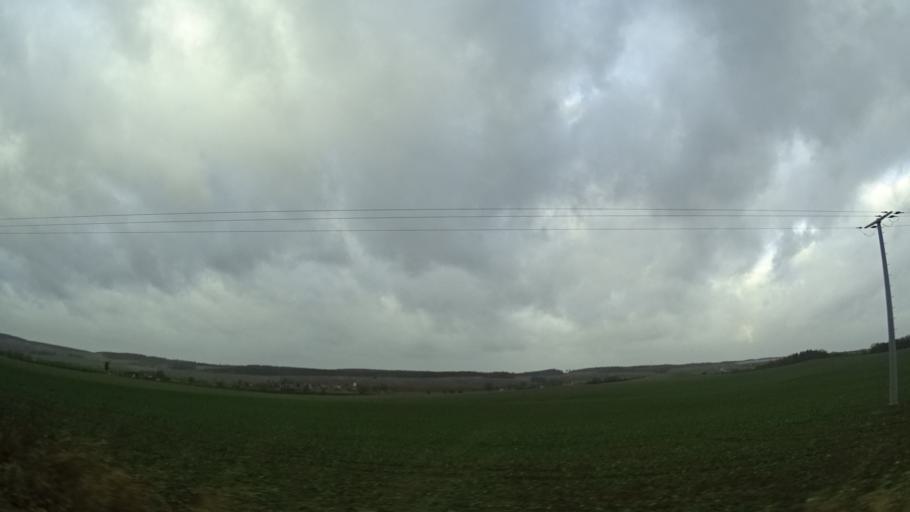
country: DE
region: Thuringia
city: Miesitz
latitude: 50.7277
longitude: 11.8245
